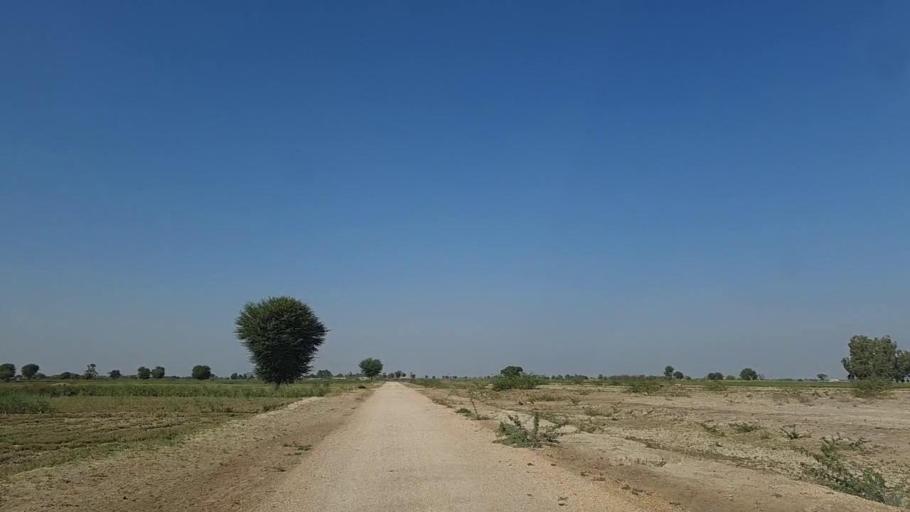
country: PK
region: Sindh
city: Pithoro
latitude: 25.4012
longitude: 69.4187
